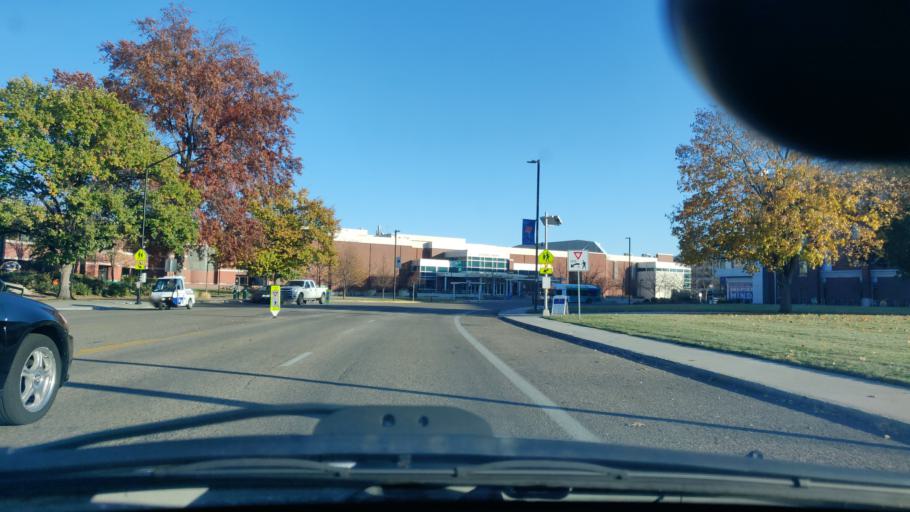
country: US
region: Idaho
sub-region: Ada County
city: Boise
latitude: 43.6024
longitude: -116.2034
